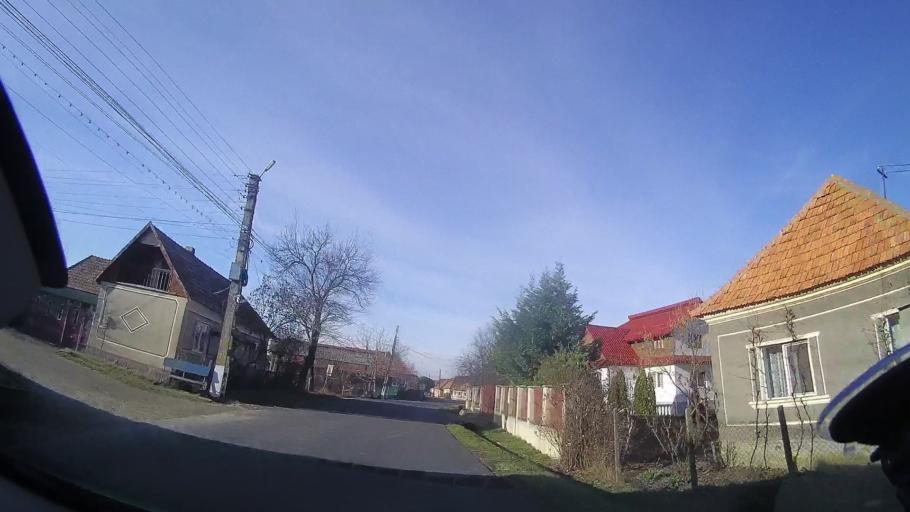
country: RO
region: Bihor
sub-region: Comuna Magesti
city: Magesti
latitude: 47.0123
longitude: 22.4444
